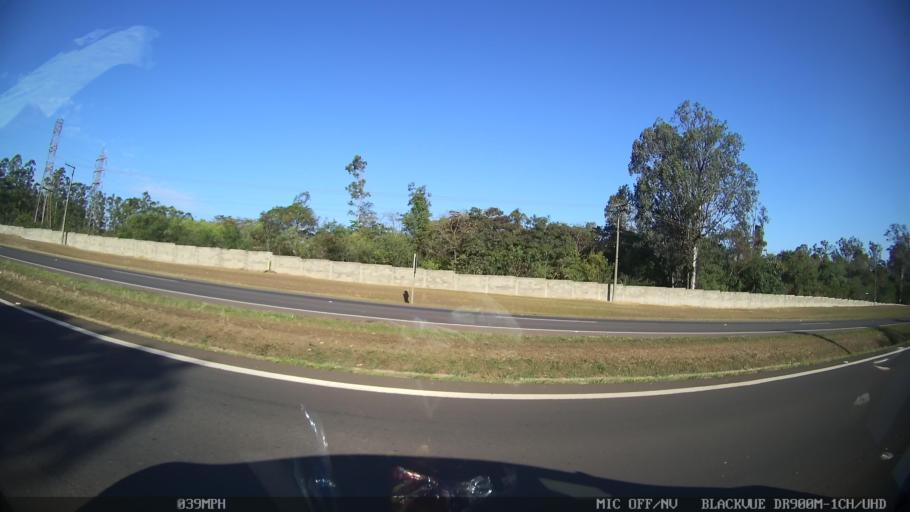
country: BR
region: Sao Paulo
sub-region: Piracicaba
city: Piracicaba
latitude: -22.6945
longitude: -47.6496
